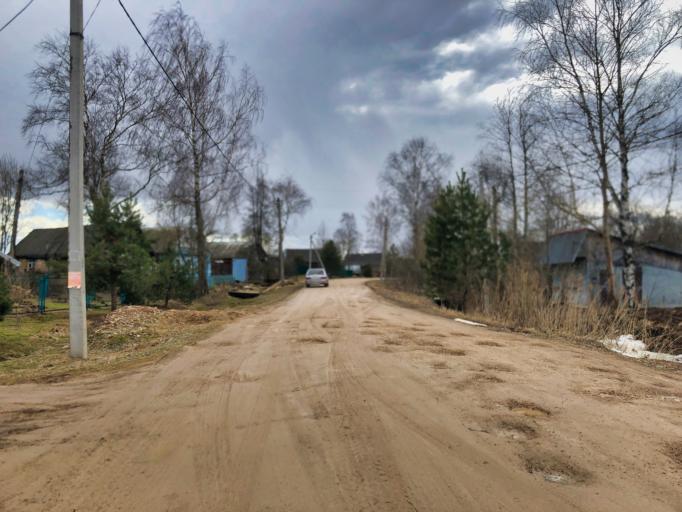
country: RU
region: Tverskaya
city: Rzhev
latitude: 56.2278
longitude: 34.3093
